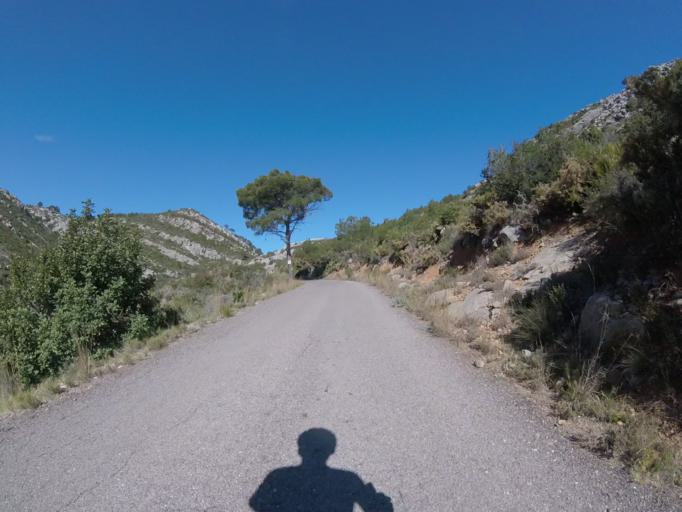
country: ES
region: Valencia
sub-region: Provincia de Castello
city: Benicassim
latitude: 40.0770
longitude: 0.1058
